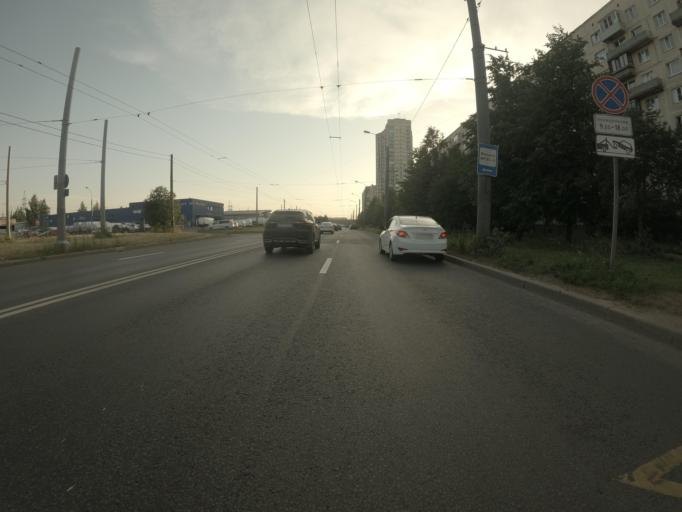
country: RU
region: St.-Petersburg
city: Krasnogvargeisky
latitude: 59.9367
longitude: 30.4815
